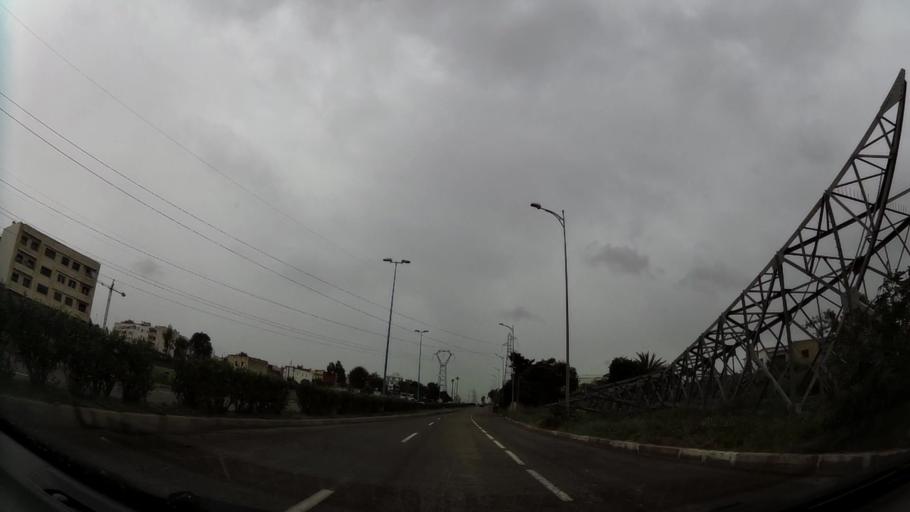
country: MA
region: Grand Casablanca
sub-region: Casablanca
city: Casablanca
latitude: 33.5380
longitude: -7.6178
